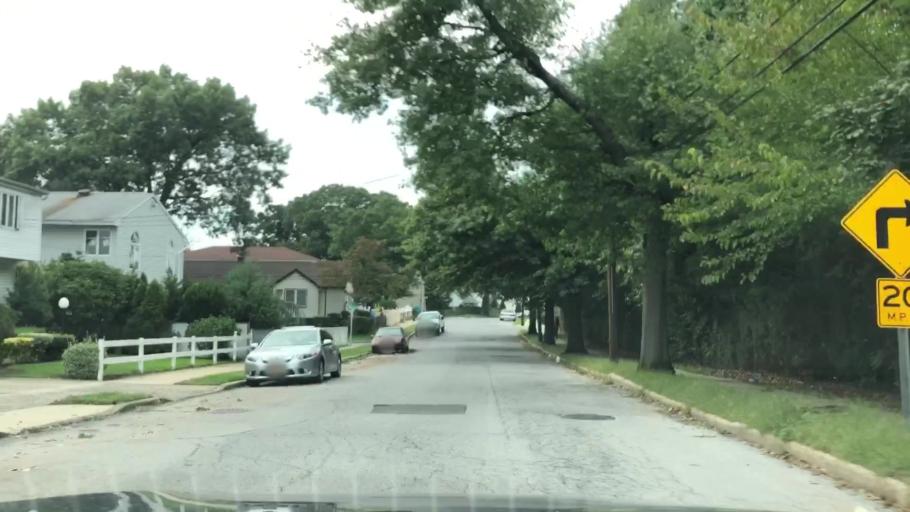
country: US
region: New York
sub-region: Nassau County
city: South Floral Park
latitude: 40.7002
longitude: -73.6984
